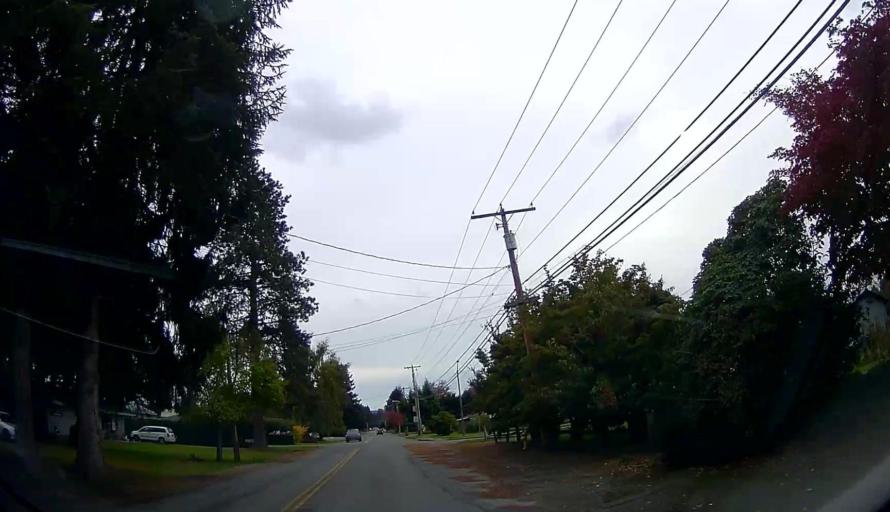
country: US
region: Washington
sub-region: Skagit County
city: Burlington
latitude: 48.4801
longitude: -122.3086
